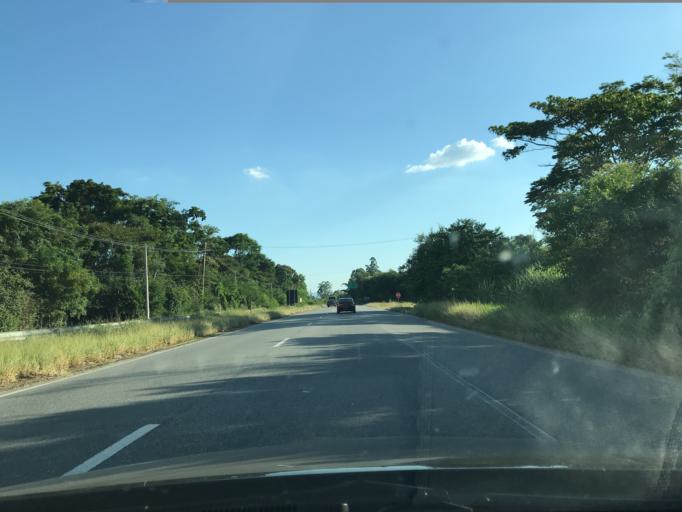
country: BR
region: Sao Paulo
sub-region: Taubate
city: Taubate
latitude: -23.0075
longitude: -45.6402
